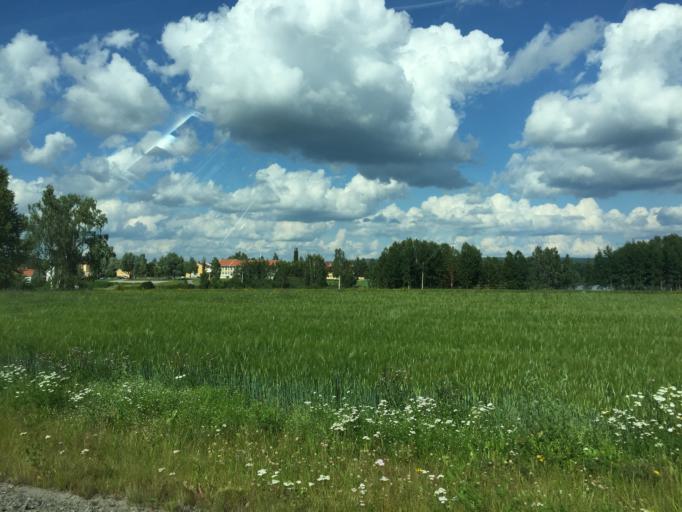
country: SE
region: Gaevleborg
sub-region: Bollnas Kommun
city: Bollnas
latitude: 61.3377
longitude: 16.3965
